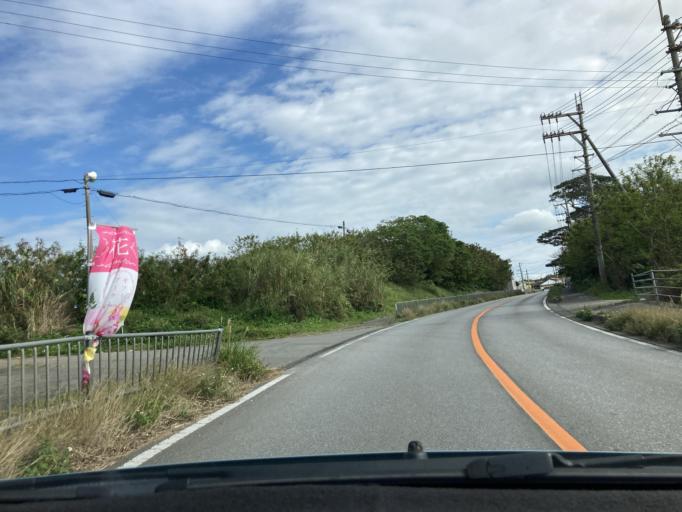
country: JP
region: Okinawa
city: Nago
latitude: 26.6990
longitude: 127.9329
